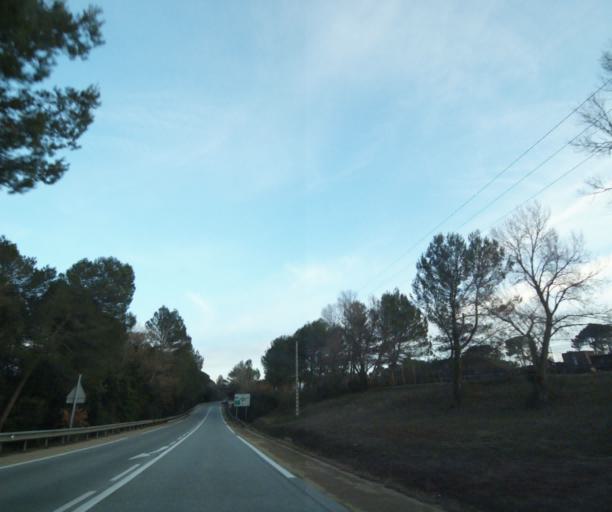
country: FR
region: Provence-Alpes-Cote d'Azur
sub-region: Departement du Var
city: La Motte
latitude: 43.4816
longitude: 6.5188
